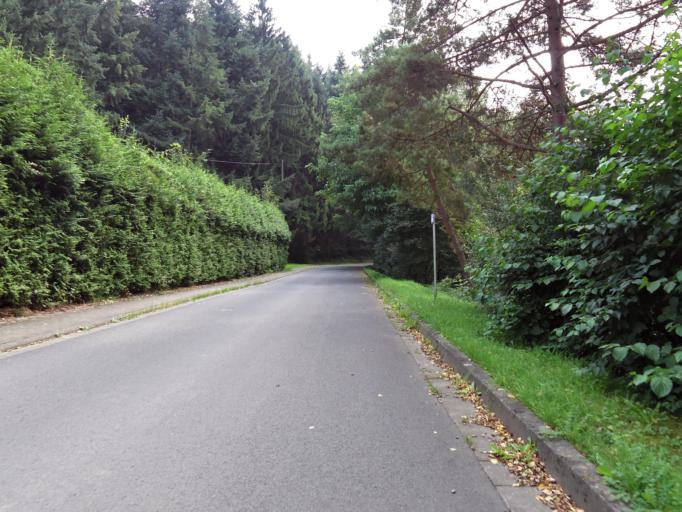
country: DE
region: Rheinland-Pfalz
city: Rockenhausen
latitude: 49.6176
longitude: 7.8233
